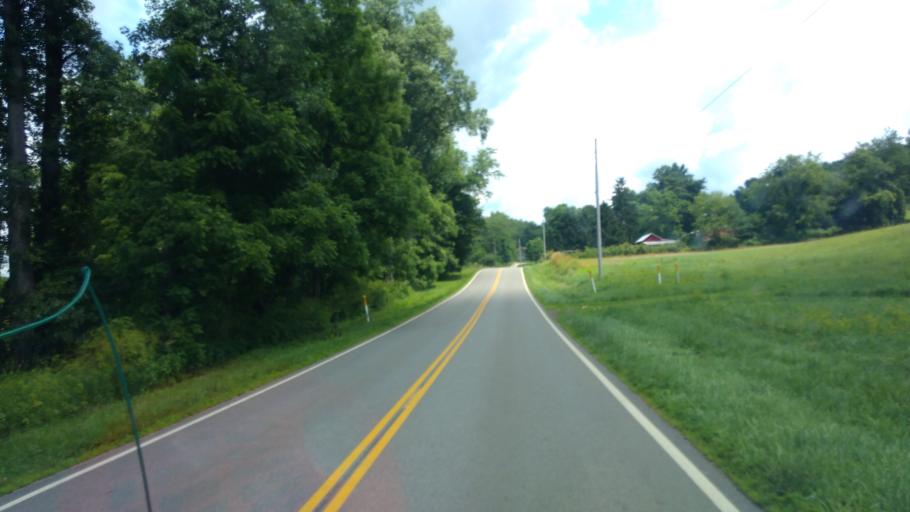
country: US
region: Ohio
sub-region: Ashland County
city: Loudonville
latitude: 40.7322
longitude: -82.2887
